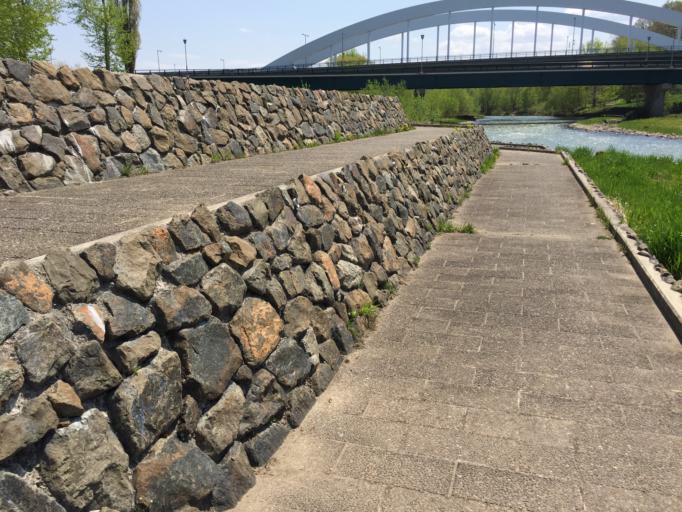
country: JP
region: Hokkaido
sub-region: Asahikawa-shi
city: Asahikawa
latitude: 43.7561
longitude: 142.3657
